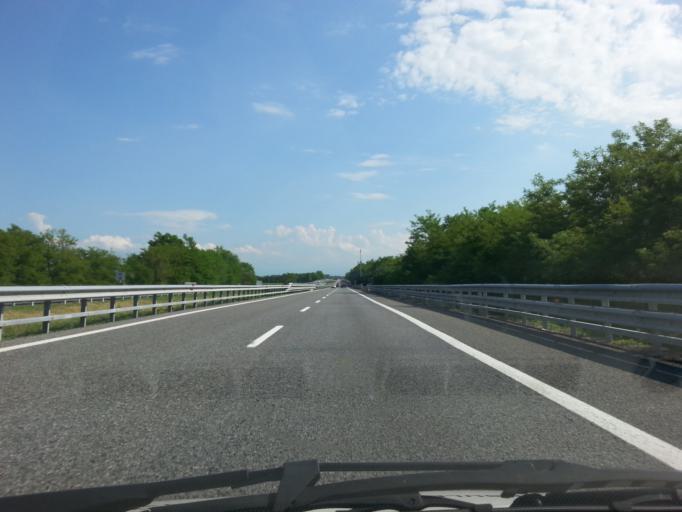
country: IT
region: Piedmont
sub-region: Provincia di Cuneo
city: Caramagna Piemonte
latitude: 44.8065
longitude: 7.7518
